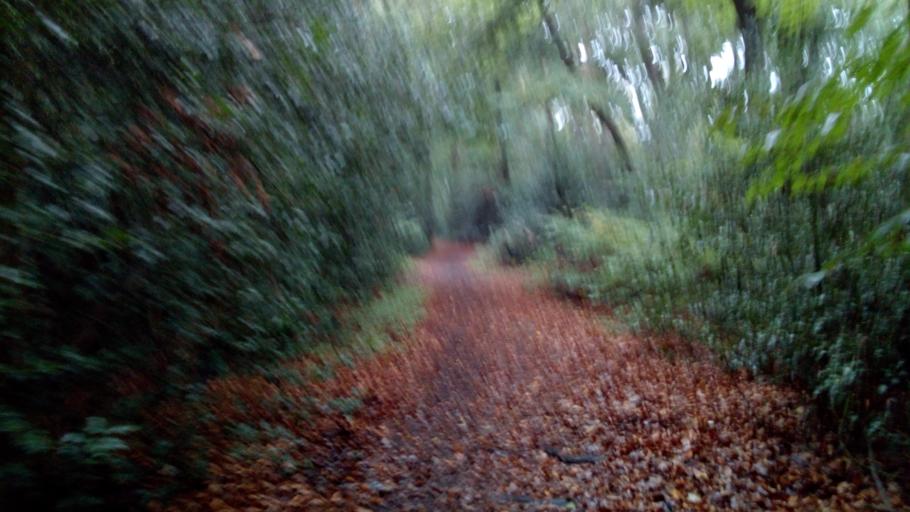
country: DE
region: North Rhine-Westphalia
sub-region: Regierungsbezirk Arnsberg
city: Bochum
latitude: 51.4429
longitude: 7.2756
